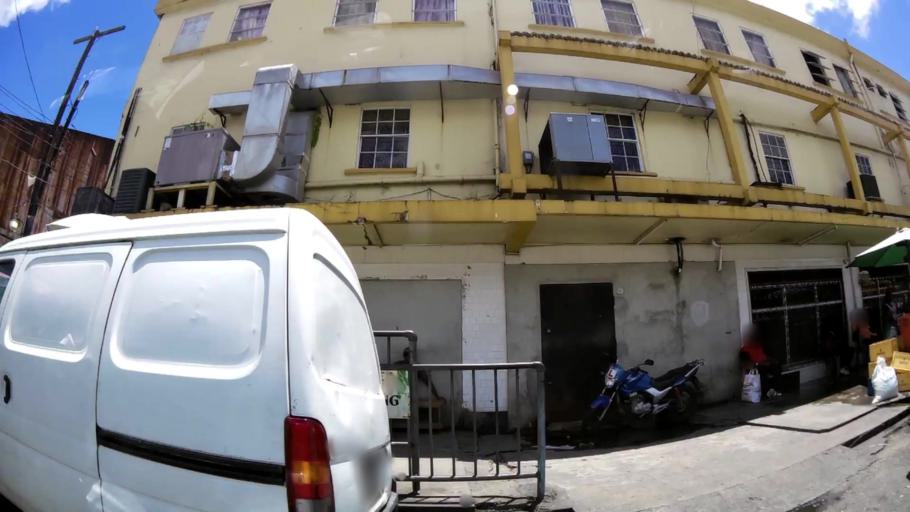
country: GY
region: Demerara-Mahaica
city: Georgetown
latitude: 6.8114
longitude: -58.1666
